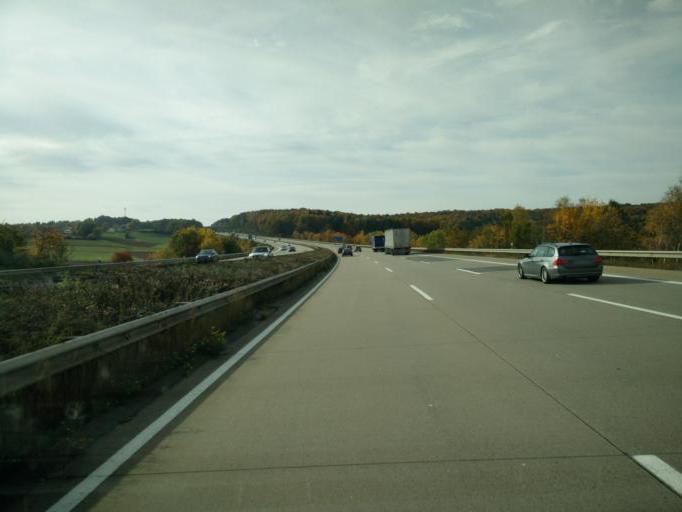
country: DE
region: Rheinland-Pfalz
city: Wattenheim
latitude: 49.5269
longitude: 8.0589
